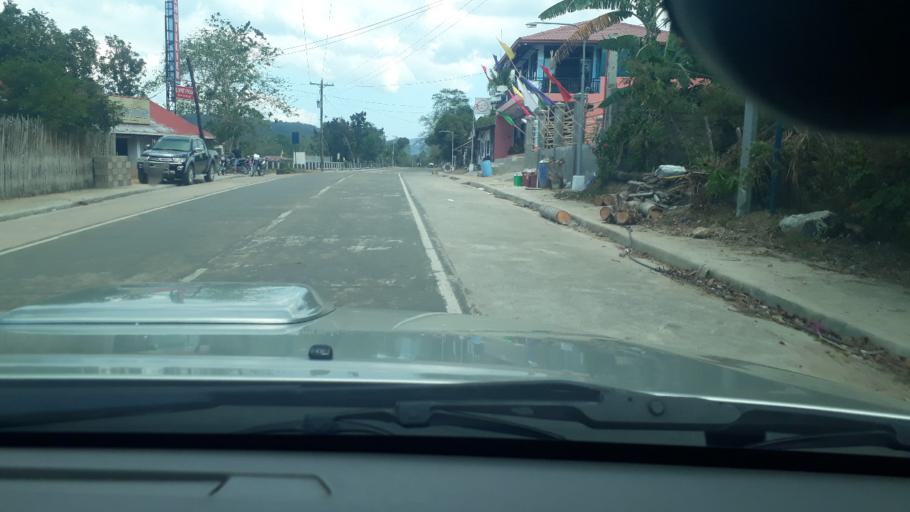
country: PH
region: Mimaropa
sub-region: Province of Palawan
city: Salvacion
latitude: 12.1313
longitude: 119.9373
